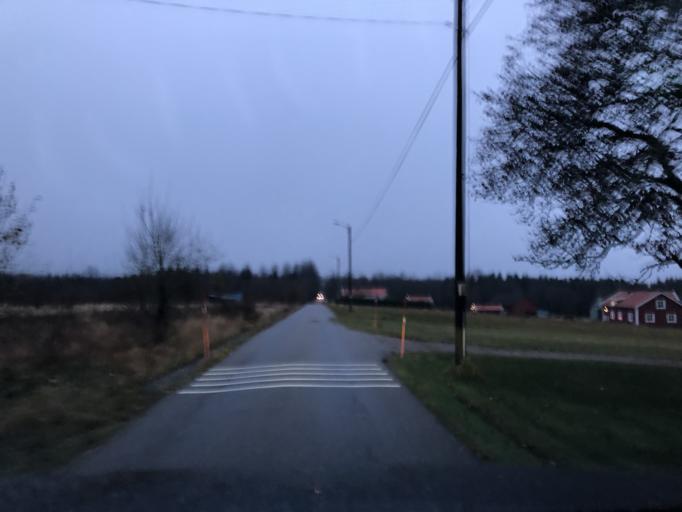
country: SE
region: Vaestra Goetaland
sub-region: Boras Kommun
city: Sjomarken
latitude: 57.7657
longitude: 12.8510
